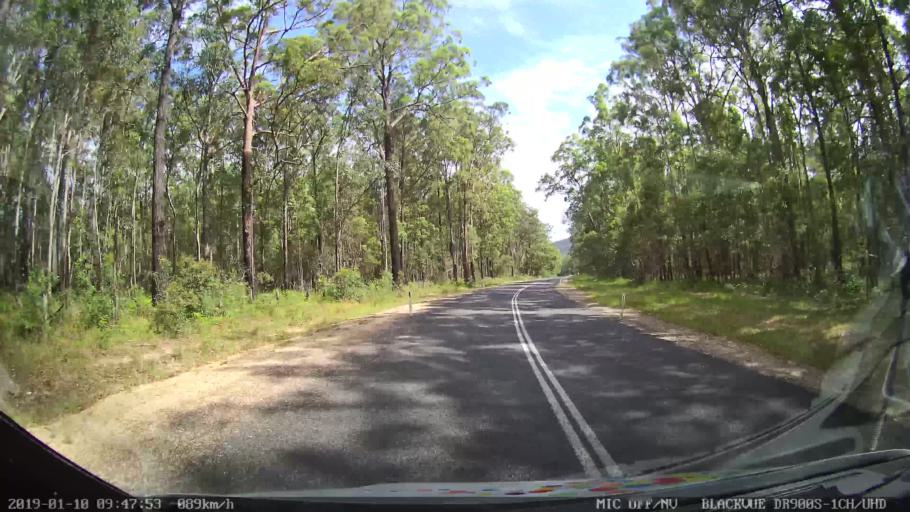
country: AU
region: New South Wales
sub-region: Coffs Harbour
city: Nana Glen
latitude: -30.0797
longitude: 152.9889
